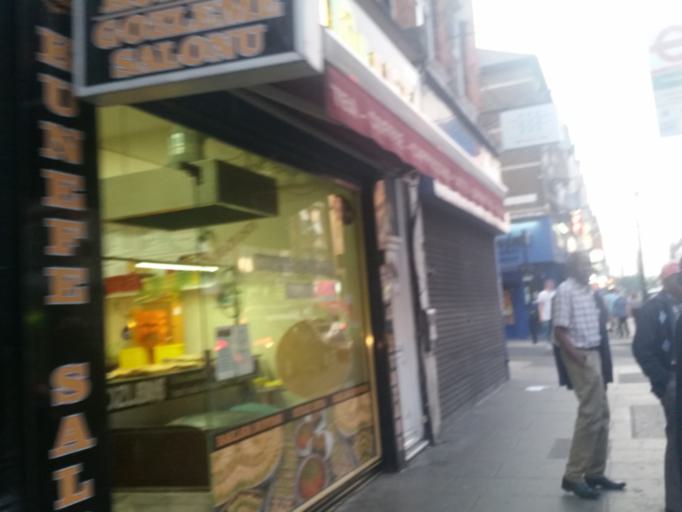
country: GB
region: England
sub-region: Greater London
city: Harringay
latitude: 51.5799
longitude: -0.0991
